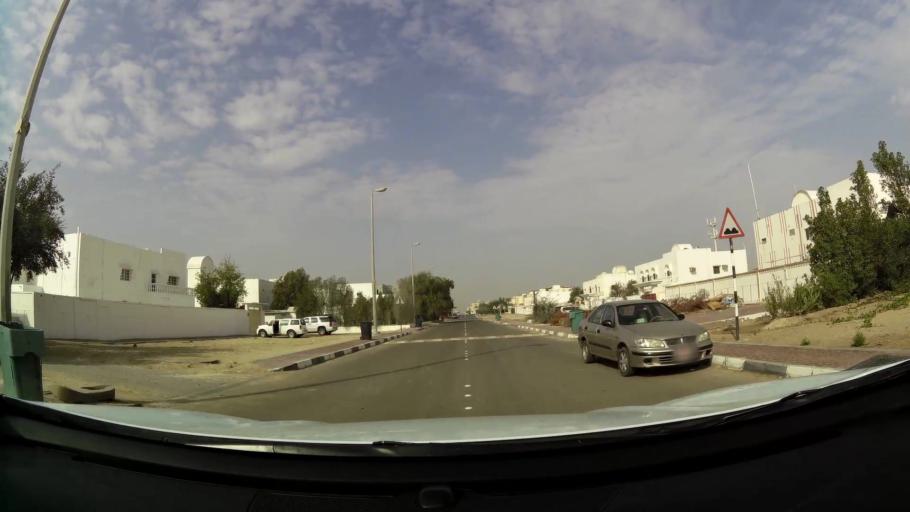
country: AE
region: Abu Dhabi
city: Abu Dhabi
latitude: 24.2540
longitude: 54.7232
